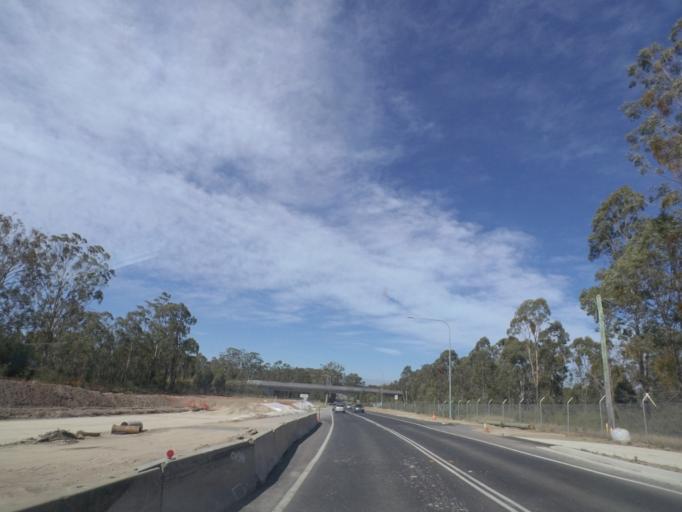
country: AU
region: New South Wales
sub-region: Campbelltown Municipality
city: Denham Court
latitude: -33.9719
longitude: 150.8648
